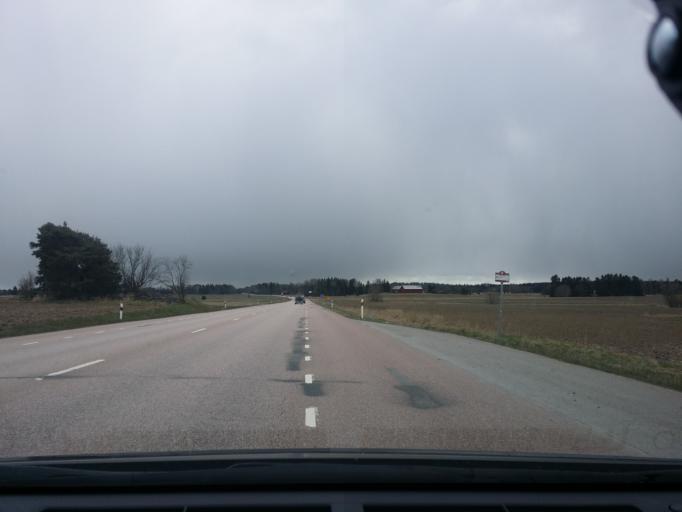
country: SE
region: Uppsala
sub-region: Enkopings Kommun
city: Enkoping
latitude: 59.6853
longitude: 17.0379
